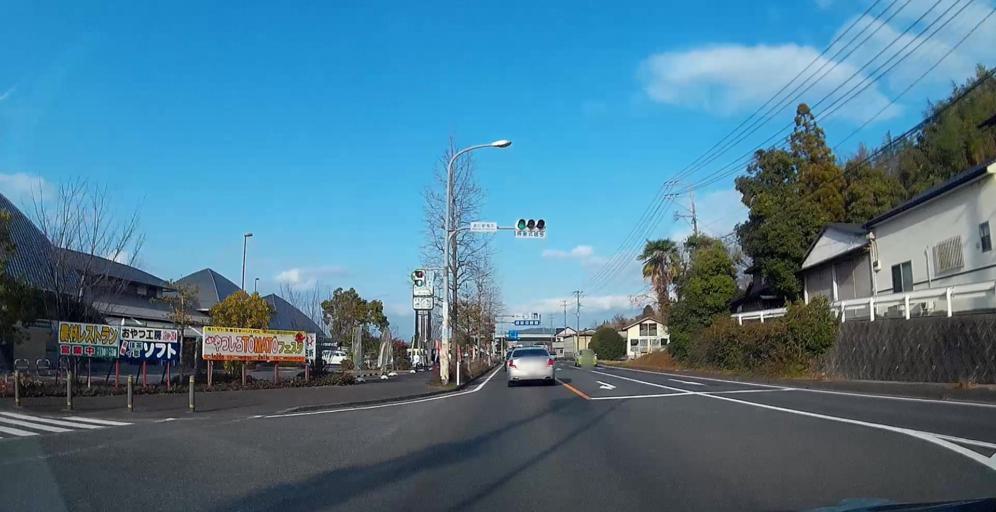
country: JP
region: Kumamoto
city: Matsubase
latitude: 32.5764
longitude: 130.6949
